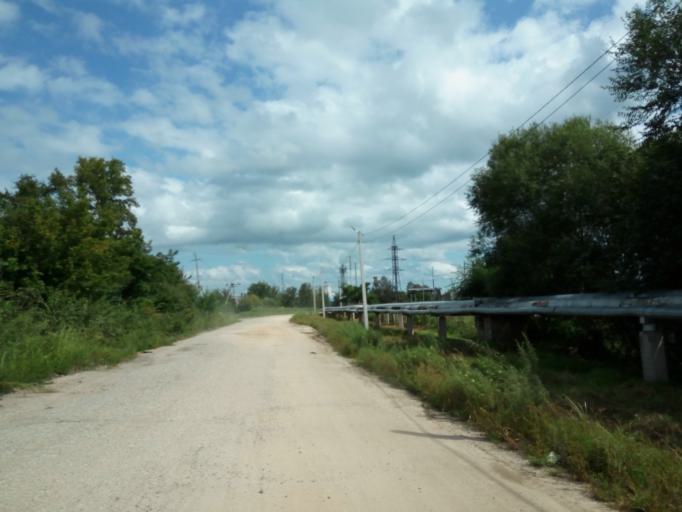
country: RU
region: Primorskiy
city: Dal'nerechensk
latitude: 45.9509
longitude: 133.8203
